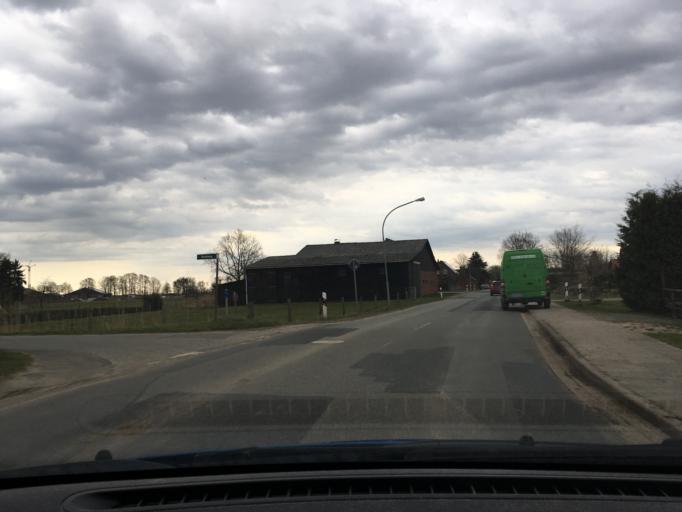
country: DE
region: Lower Saxony
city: Drage
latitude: 53.3764
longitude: 10.2858
